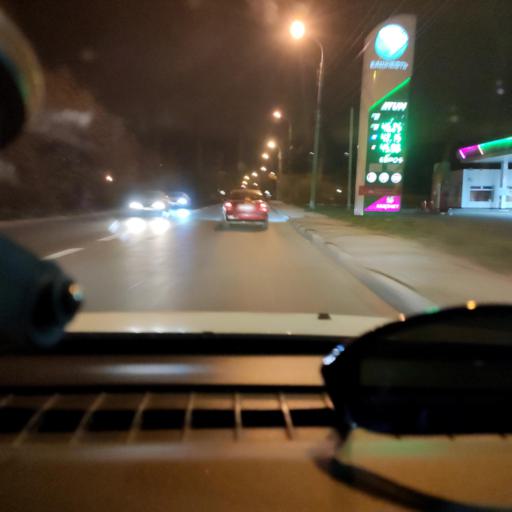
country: RU
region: Samara
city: Rozhdestveno
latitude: 53.1630
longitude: 50.0762
